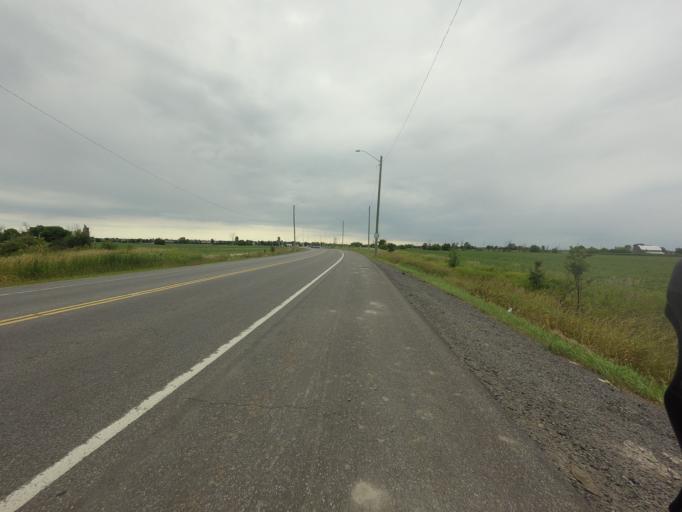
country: CA
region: Ontario
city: Bells Corners
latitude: 45.3014
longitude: -75.7259
